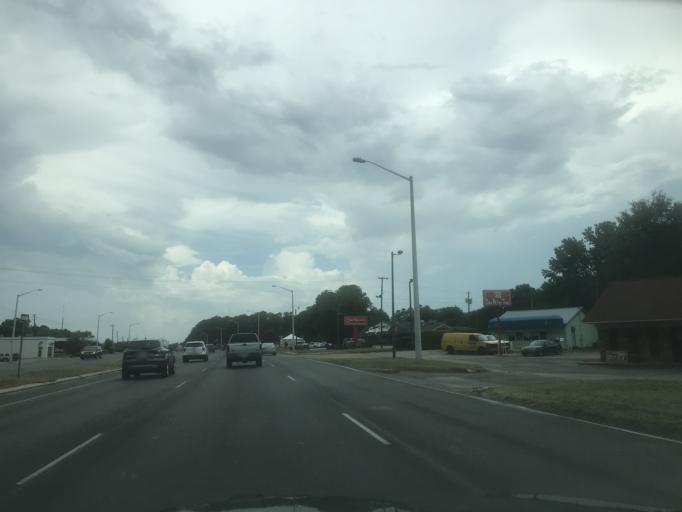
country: US
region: North Carolina
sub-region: Johnston County
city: Clayton
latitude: 35.6424
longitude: -78.4518
